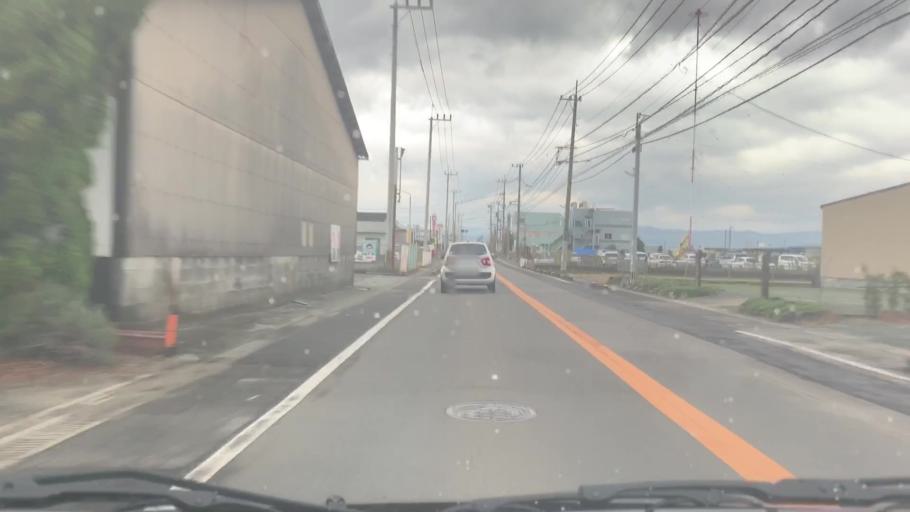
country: JP
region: Saga Prefecture
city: Saga-shi
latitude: 33.2488
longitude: 130.2653
